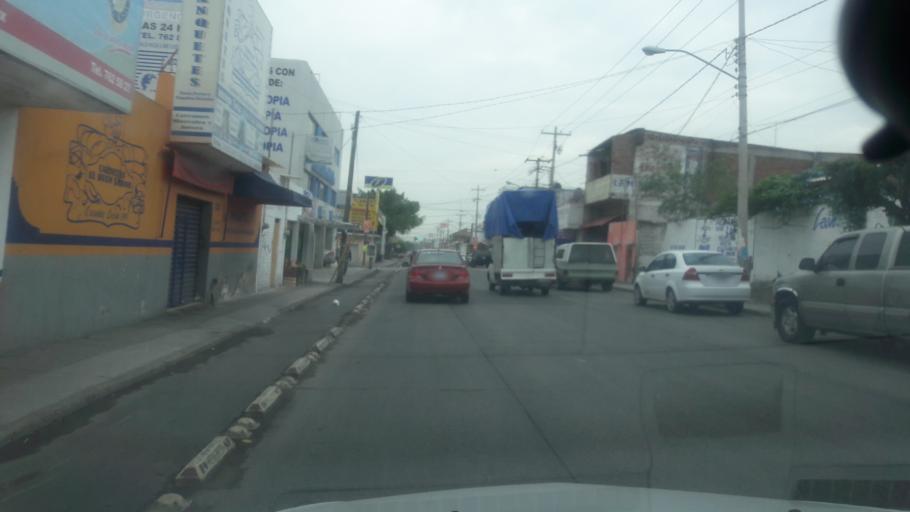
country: MX
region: Guanajuato
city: Leon
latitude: 21.1373
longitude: -101.7031
